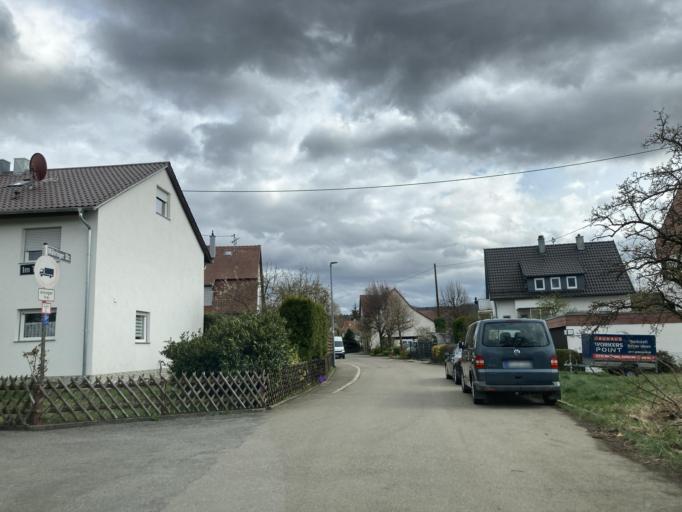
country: DE
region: Baden-Wuerttemberg
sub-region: Tuebingen Region
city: Wannweil
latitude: 48.4785
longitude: 9.1316
